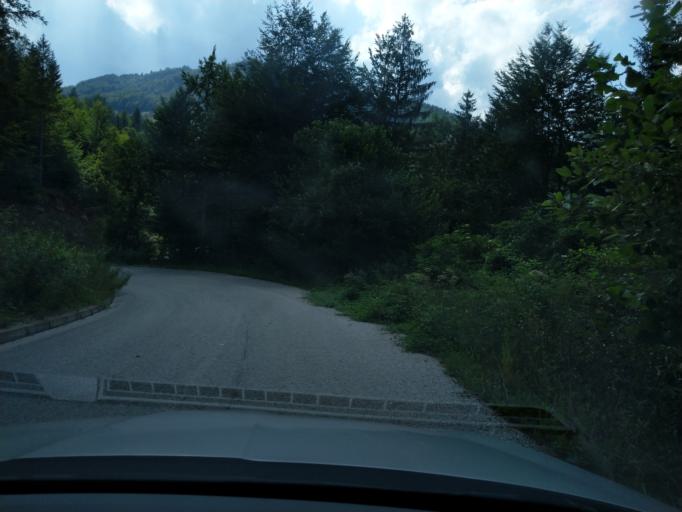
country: RS
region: Central Serbia
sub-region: Zlatiborski Okrug
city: Nova Varos
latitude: 43.5798
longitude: 19.8847
